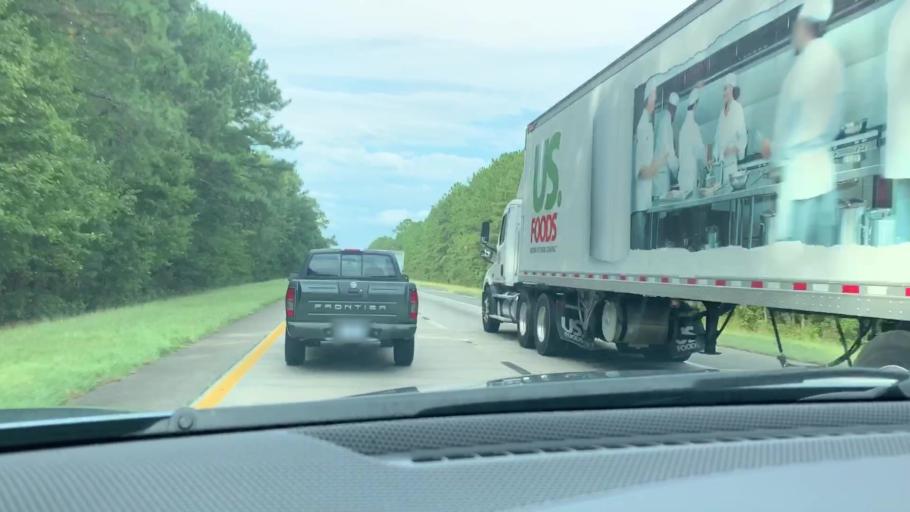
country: US
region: South Carolina
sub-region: Colleton County
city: Walterboro
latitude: 32.9878
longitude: -80.6722
